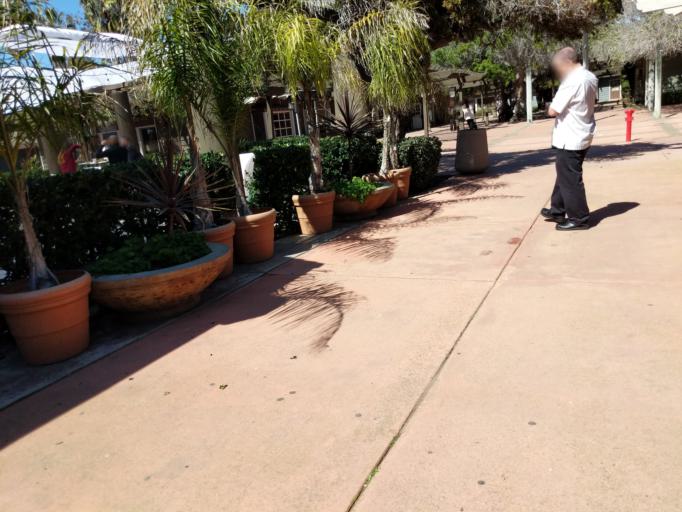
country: US
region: California
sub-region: San Diego County
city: San Diego
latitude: 32.7620
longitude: -117.2340
